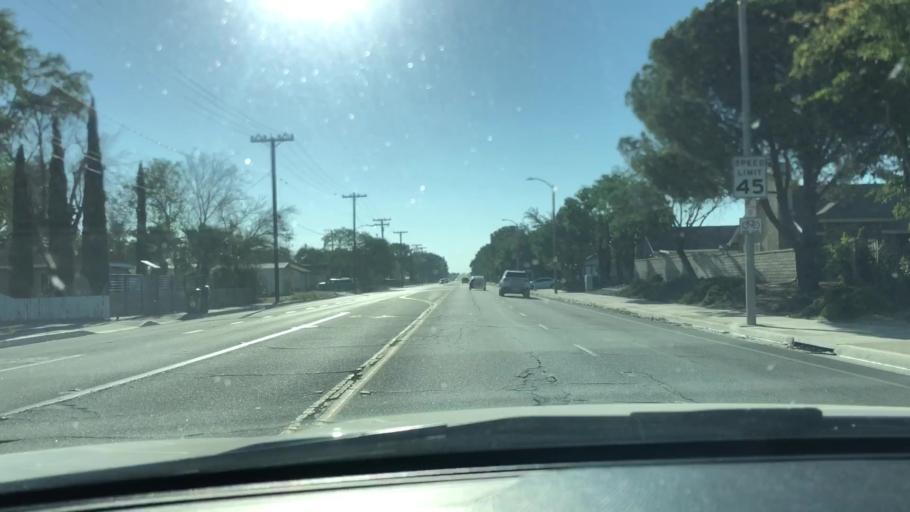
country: US
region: California
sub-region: Los Angeles County
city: Lancaster
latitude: 34.6677
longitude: -118.1651
